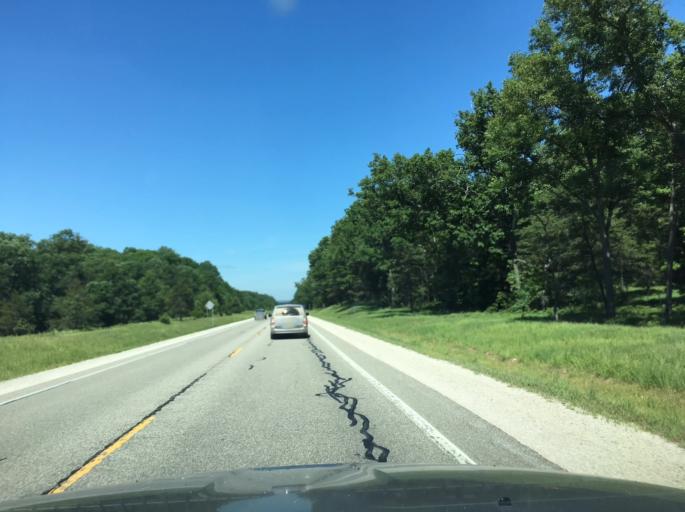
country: US
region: Michigan
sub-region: Lake County
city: Baldwin
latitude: 43.8945
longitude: -85.6831
